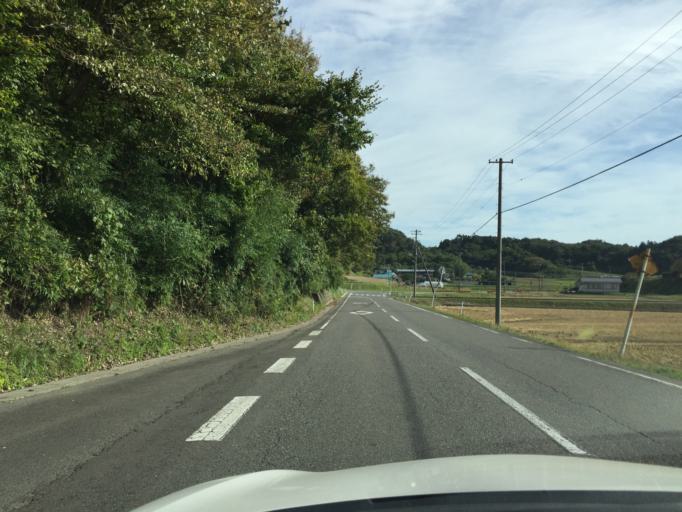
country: JP
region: Fukushima
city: Miharu
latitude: 37.4681
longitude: 140.4932
